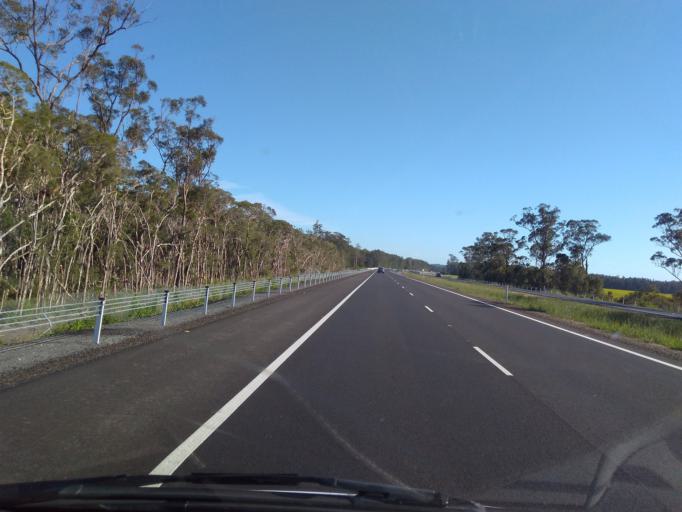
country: AU
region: New South Wales
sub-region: Port Macquarie-Hastings
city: North Shore
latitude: -31.3513
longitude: 152.8069
